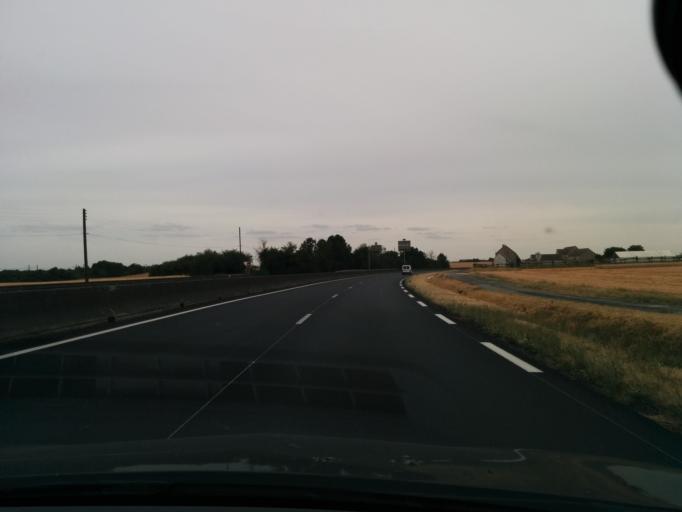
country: FR
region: Ile-de-France
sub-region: Departement de l'Essonne
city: Angerville
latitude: 48.3025
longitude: 1.9921
